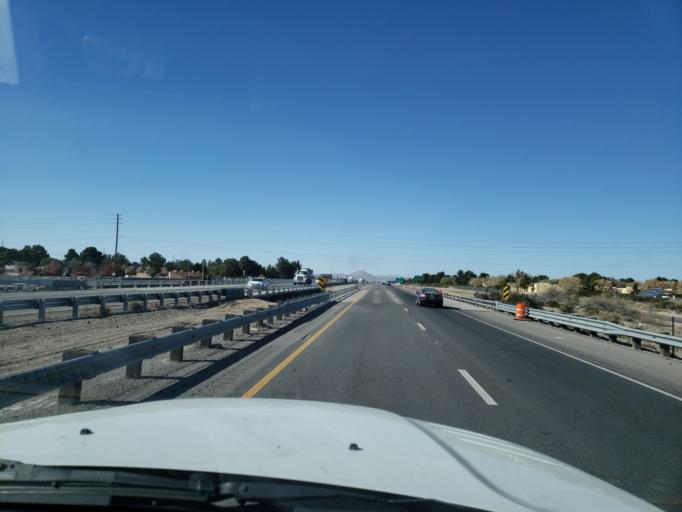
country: US
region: New Mexico
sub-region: Dona Ana County
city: University Park
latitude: 32.2688
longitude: -106.7449
